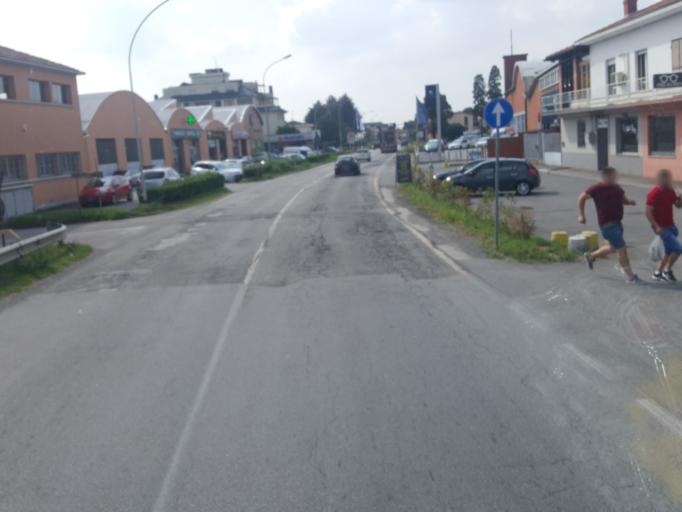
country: IT
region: Lombardy
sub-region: Citta metropolitana di Milano
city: Abbiategrasso
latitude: 45.3878
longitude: 8.9218
